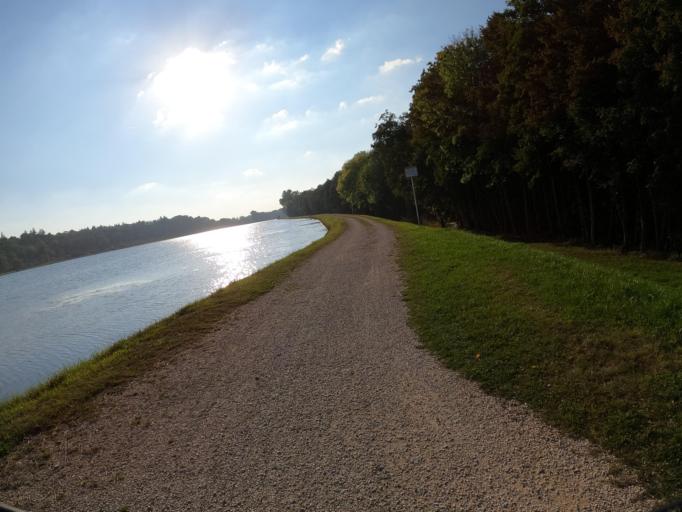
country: DE
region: Bavaria
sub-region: Swabia
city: Leipheim
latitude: 48.4438
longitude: 10.1931
